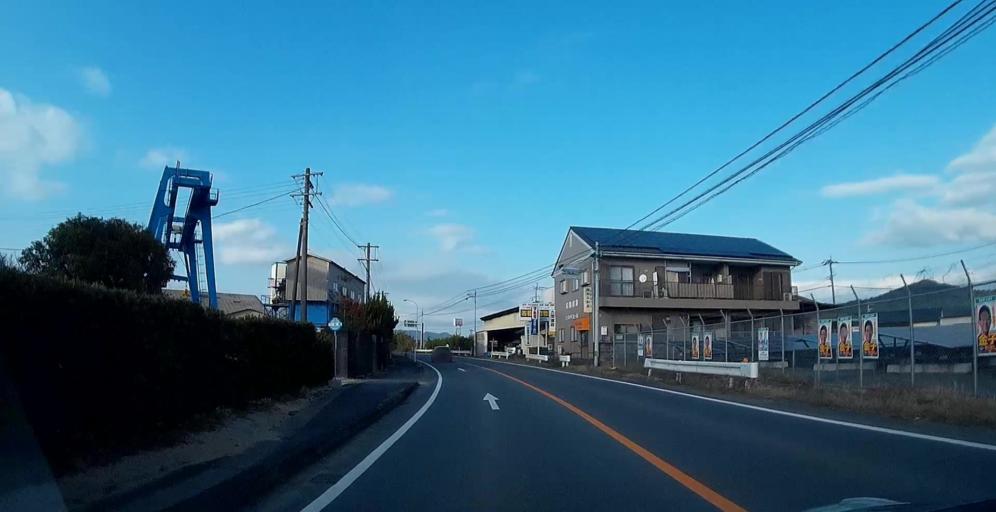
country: JP
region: Kumamoto
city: Matsubase
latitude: 32.6093
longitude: 130.7055
